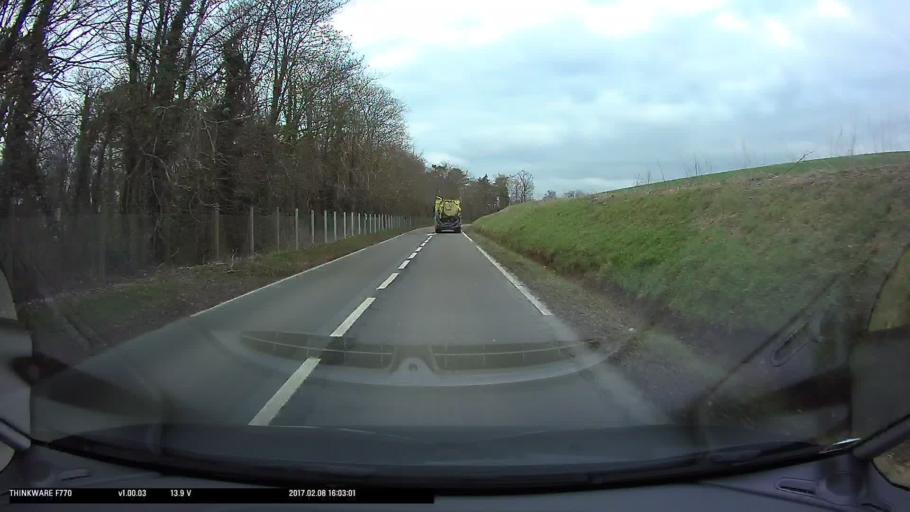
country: FR
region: Ile-de-France
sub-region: Departement du Val-d'Oise
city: Us
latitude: 49.1056
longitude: 1.9718
